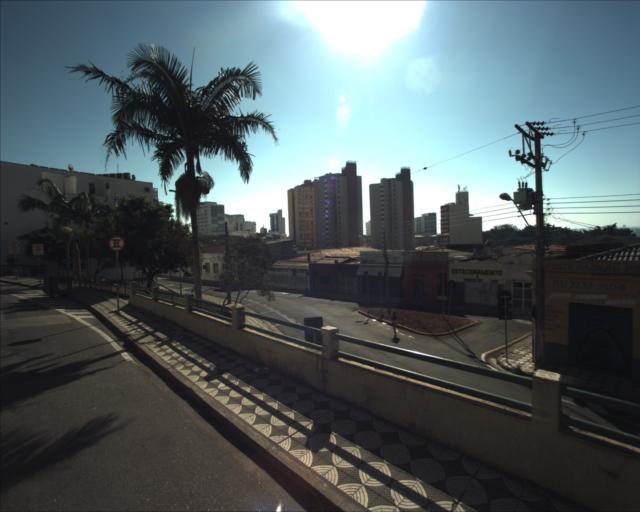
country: BR
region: Sao Paulo
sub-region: Sorocaba
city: Sorocaba
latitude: -23.5024
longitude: -47.4571
